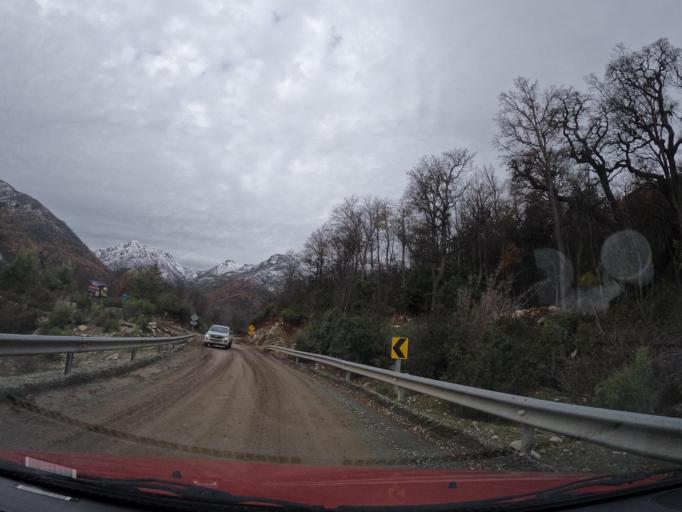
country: CL
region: Maule
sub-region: Provincia de Linares
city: Colbun
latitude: -35.8586
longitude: -71.1502
